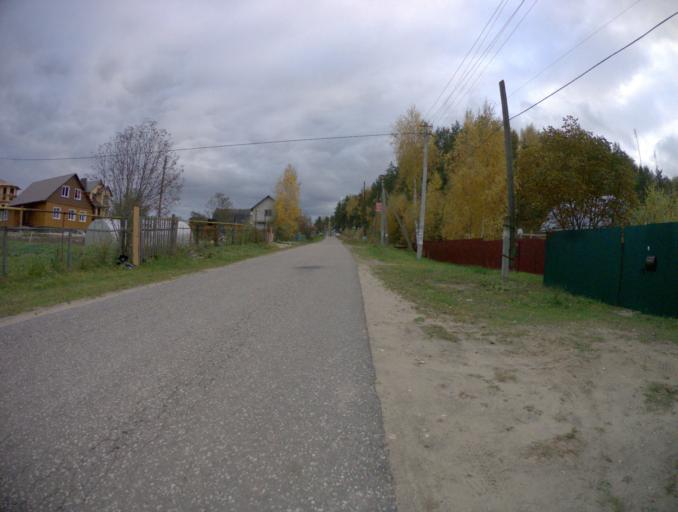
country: RU
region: Vladimir
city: Kommunar
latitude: 56.0758
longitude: 40.4914
